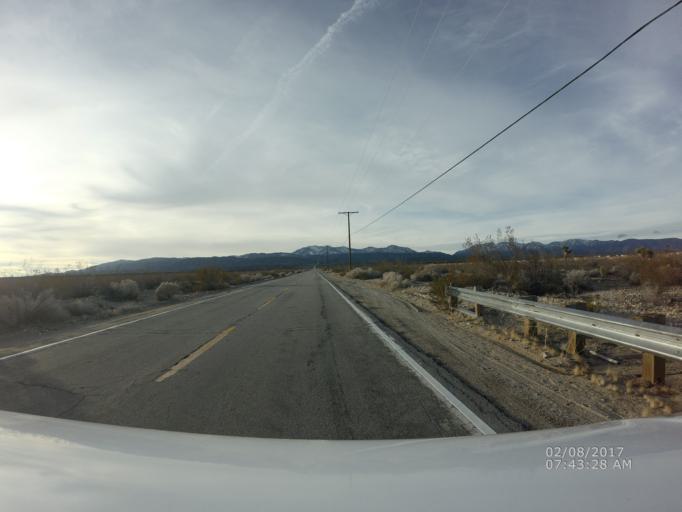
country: US
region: California
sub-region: Los Angeles County
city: Lake Los Angeles
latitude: 34.4972
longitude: -117.7652
